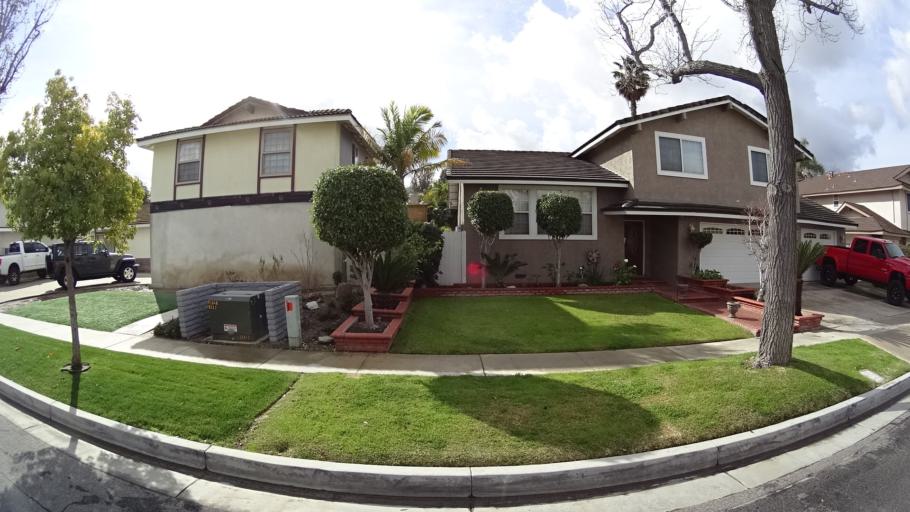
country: US
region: California
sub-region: Orange County
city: Villa Park
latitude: 33.8493
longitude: -117.7839
